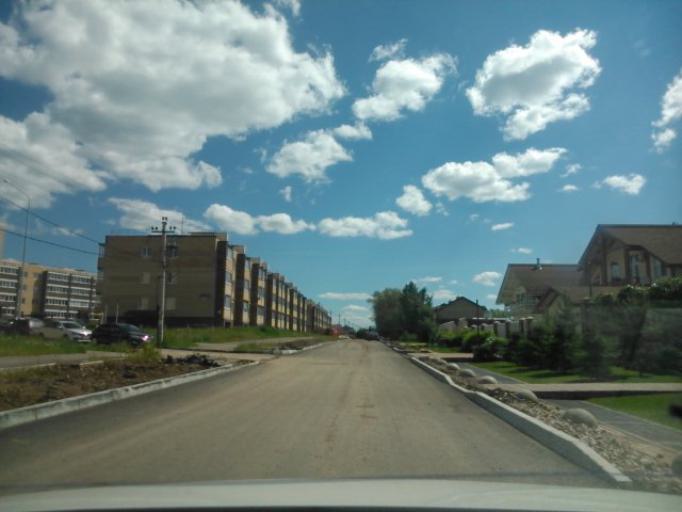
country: RU
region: Perm
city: Perm
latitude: 58.0021
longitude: 56.3348
